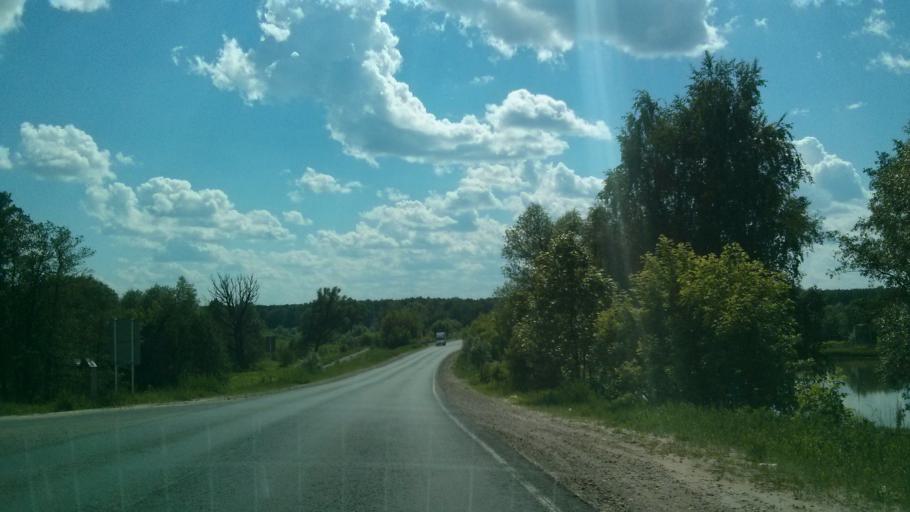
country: RU
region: Vladimir
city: Murom
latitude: 55.5253
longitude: 41.9539
